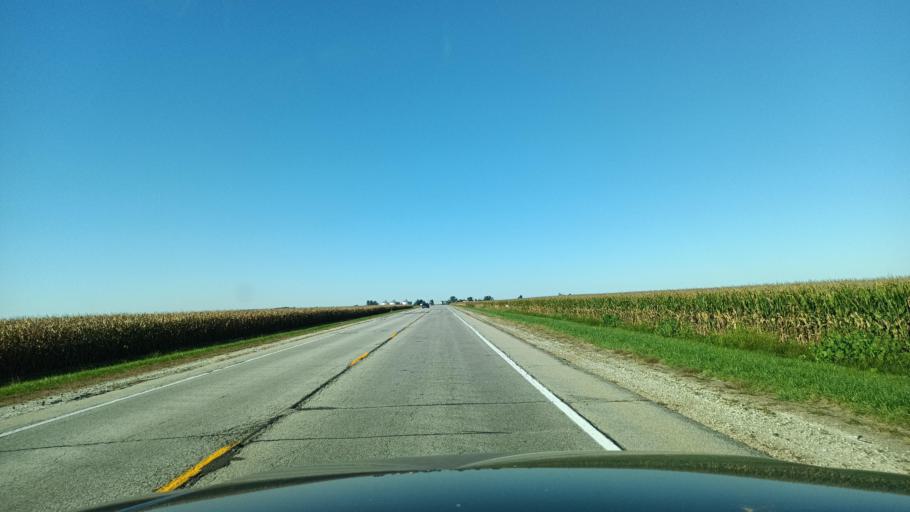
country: US
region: Illinois
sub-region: Warren County
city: Monmouth
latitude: 40.8870
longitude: -90.6722
